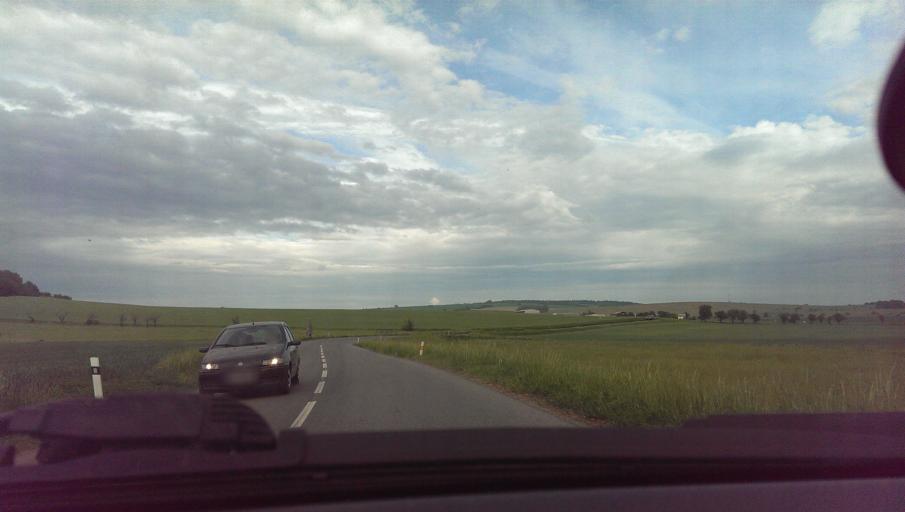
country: CZ
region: Zlin
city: Kvasice
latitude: 49.2485
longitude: 17.4534
